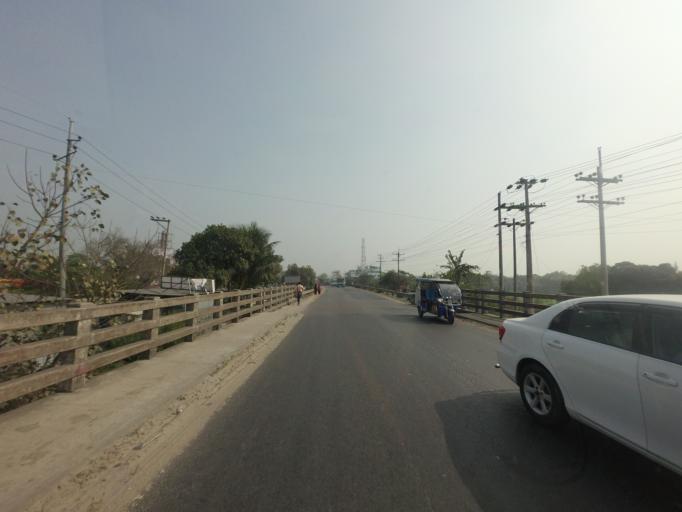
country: BD
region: Dhaka
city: Narsingdi
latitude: 23.8180
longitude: 90.5985
